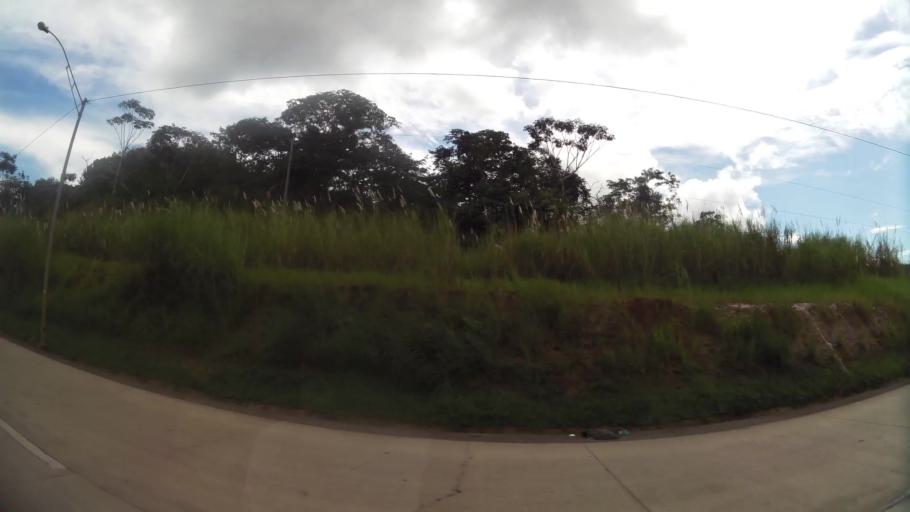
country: PA
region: Panama
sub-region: Distrito Arraijan
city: Arraijan
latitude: 8.9620
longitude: -79.6542
